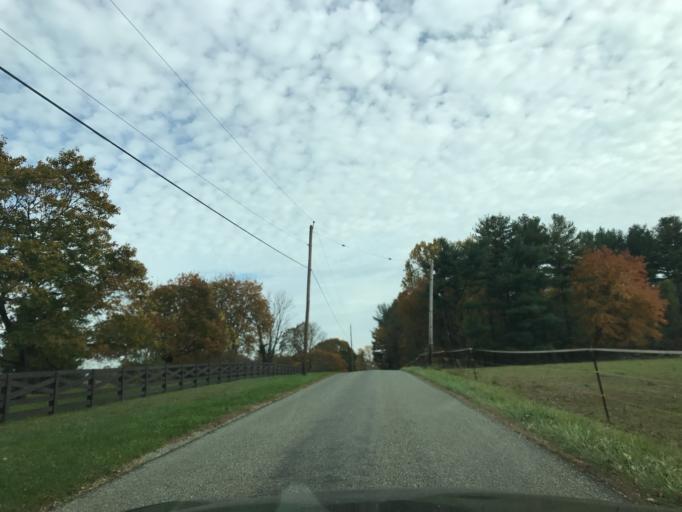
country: US
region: Maryland
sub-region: Harford County
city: Joppatowne
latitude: 39.4868
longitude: -76.3605
